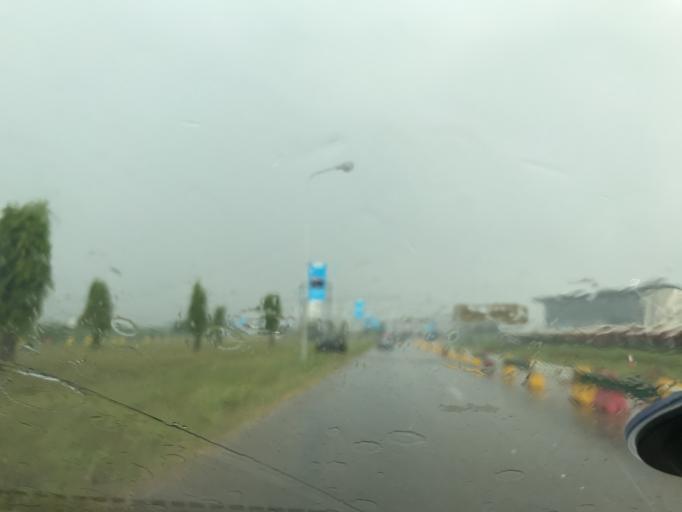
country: NG
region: Lagos
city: Oshodi
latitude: 6.5730
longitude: 3.3214
